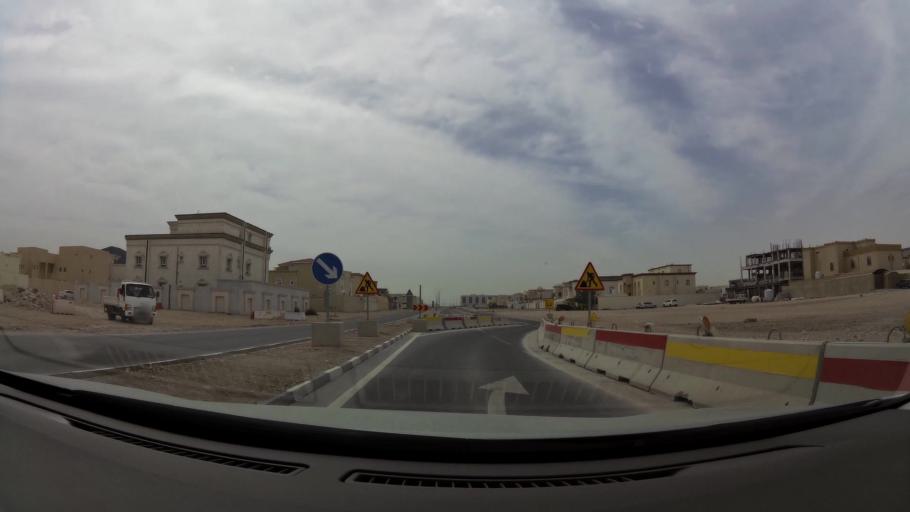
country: QA
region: Al Wakrah
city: Al Wukayr
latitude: 25.2080
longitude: 51.4722
